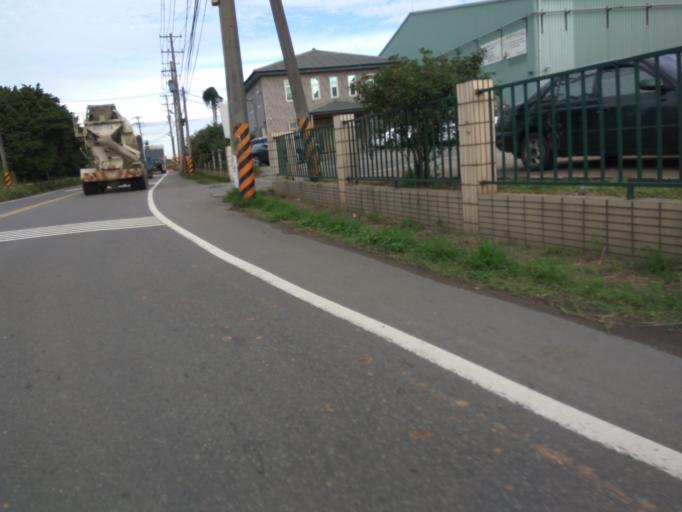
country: TW
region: Taiwan
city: Daxi
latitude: 24.9418
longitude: 121.1550
